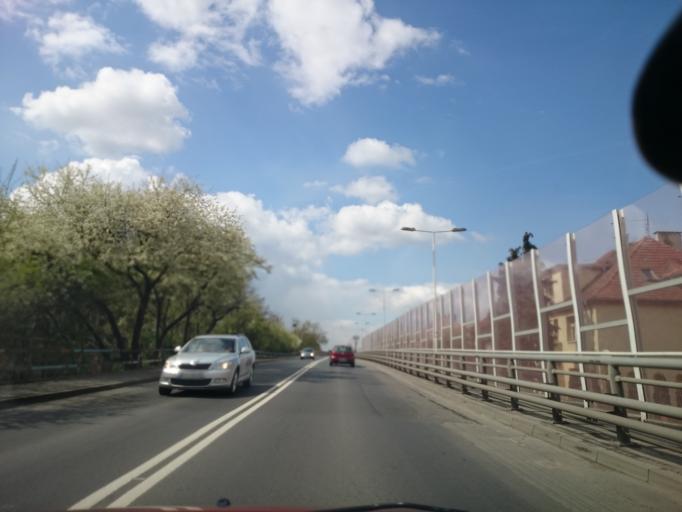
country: PL
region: Opole Voivodeship
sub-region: Powiat opolski
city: Opole
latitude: 50.6560
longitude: 17.9506
